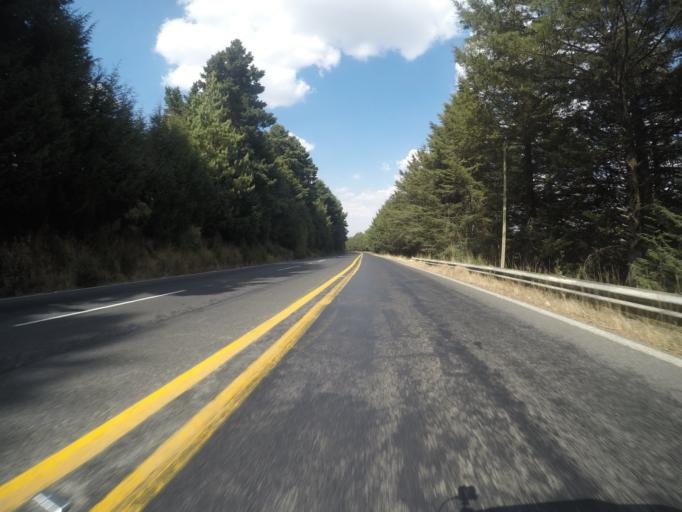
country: MX
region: Mexico
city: Cerro La Calera
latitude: 19.2157
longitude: -99.8023
